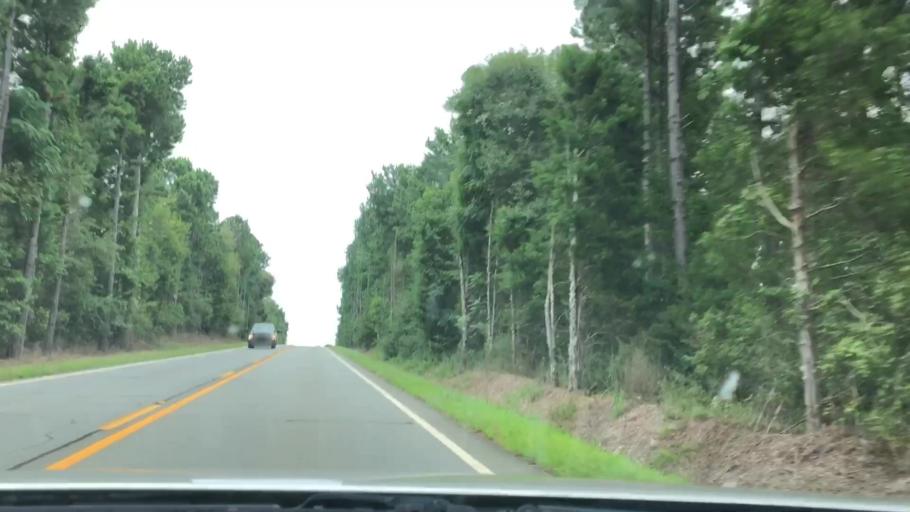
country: US
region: Georgia
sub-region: Pike County
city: Zebulon
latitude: 33.0768
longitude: -84.4540
